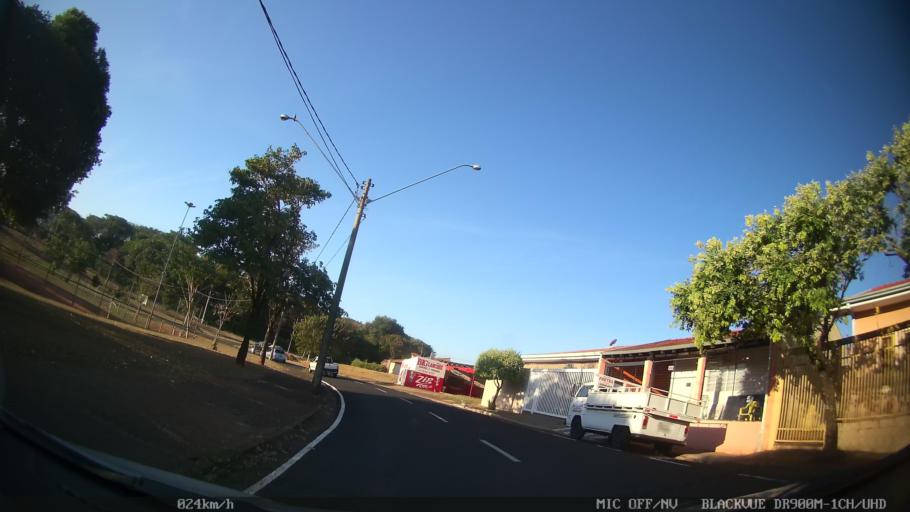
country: BR
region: Sao Paulo
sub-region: Sao Jose Do Rio Preto
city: Sao Jose do Rio Preto
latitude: -20.7883
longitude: -49.3614
